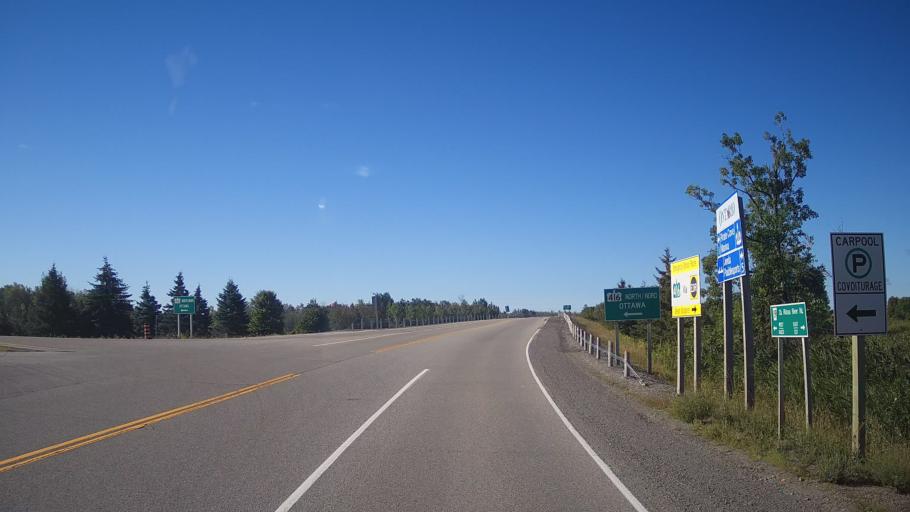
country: CA
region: Ontario
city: Bells Corners
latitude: 45.0835
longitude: -75.6322
